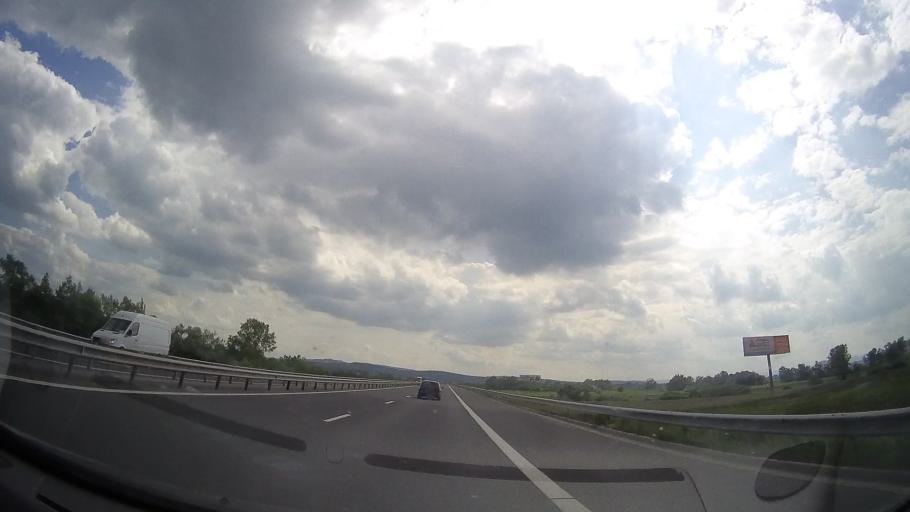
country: RO
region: Hunedoara
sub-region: Comuna Turdas
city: Pricaz
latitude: 45.8639
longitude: 23.1524
